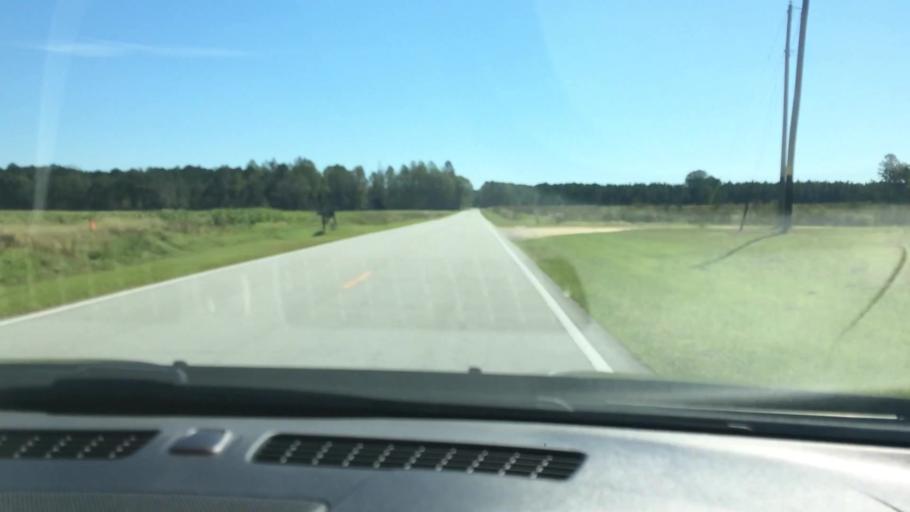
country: US
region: North Carolina
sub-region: Pitt County
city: Grifton
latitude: 35.3392
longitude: -77.3105
